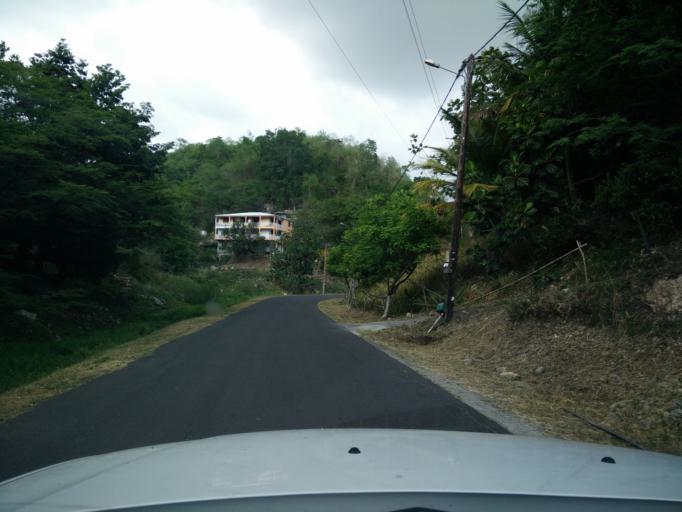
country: GP
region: Guadeloupe
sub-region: Guadeloupe
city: Le Gosier
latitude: 16.2235
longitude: -61.4656
